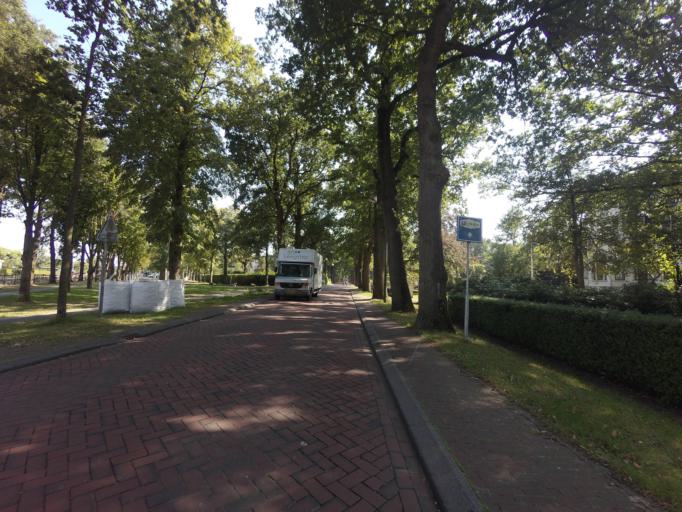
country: NL
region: Groningen
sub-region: Gemeente Zuidhorn
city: Zuidhorn
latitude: 53.2489
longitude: 6.4041
